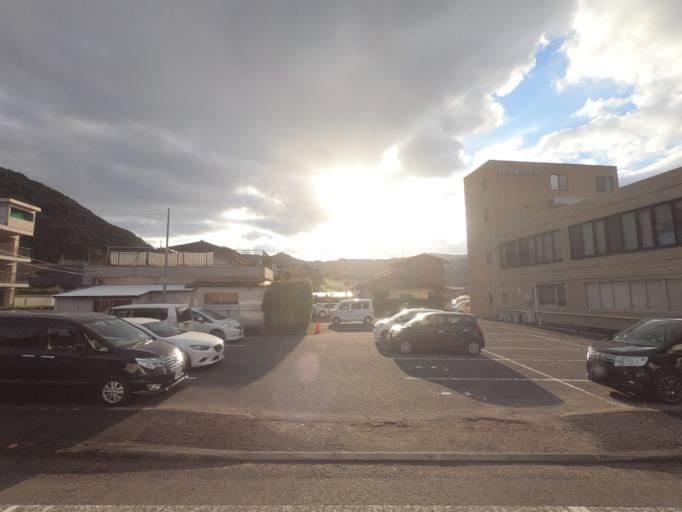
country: JP
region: Kumamoto
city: Minamata
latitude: 32.2695
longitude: 130.5037
